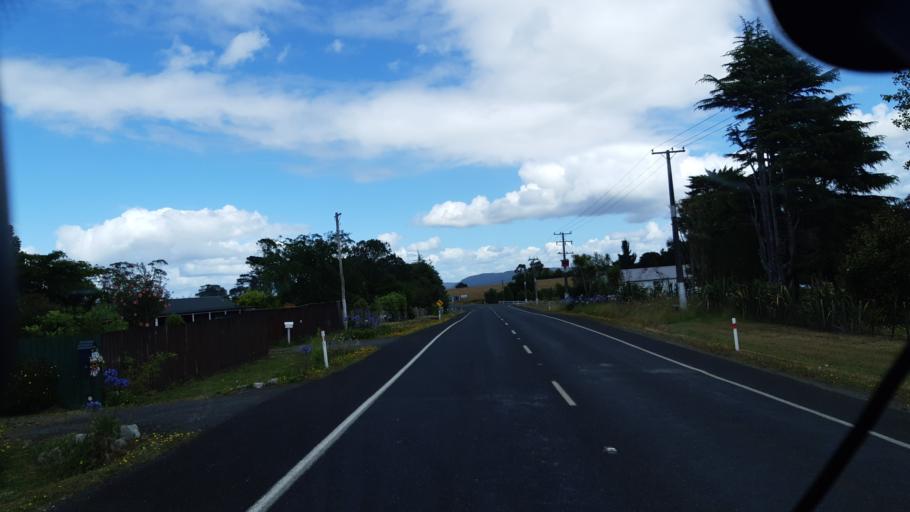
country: NZ
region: Northland
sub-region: Far North District
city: Waimate North
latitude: -35.3192
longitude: 173.7779
